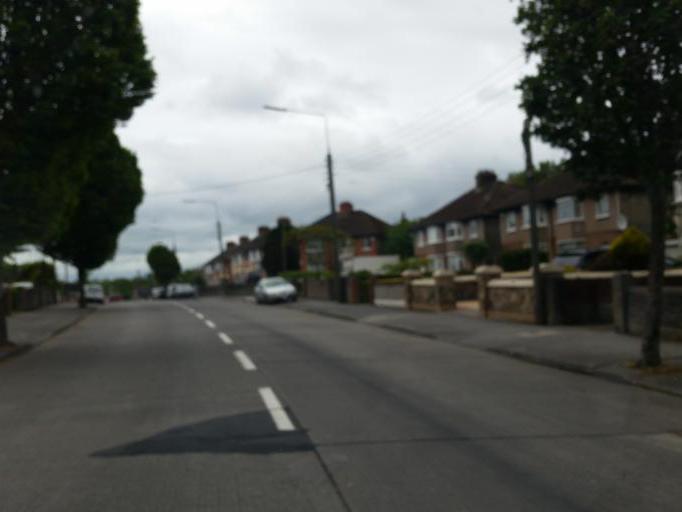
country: IE
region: Leinster
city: Cabra
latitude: 53.3660
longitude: -6.3064
